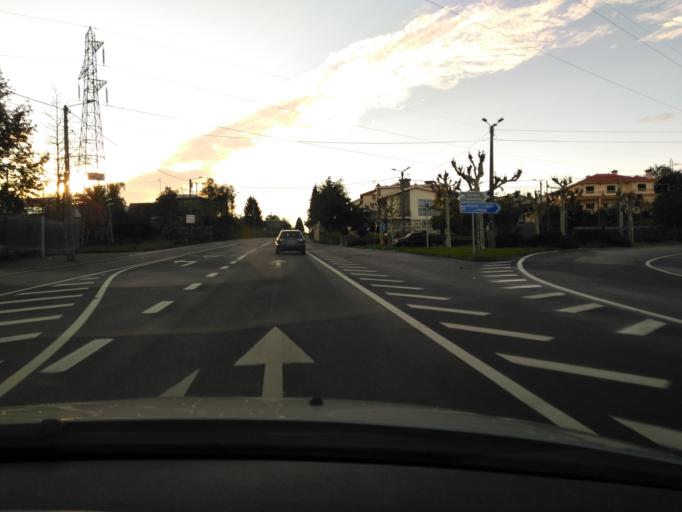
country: PT
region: Braga
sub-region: Guimaraes
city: Ponte
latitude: 41.4685
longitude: -8.3274
